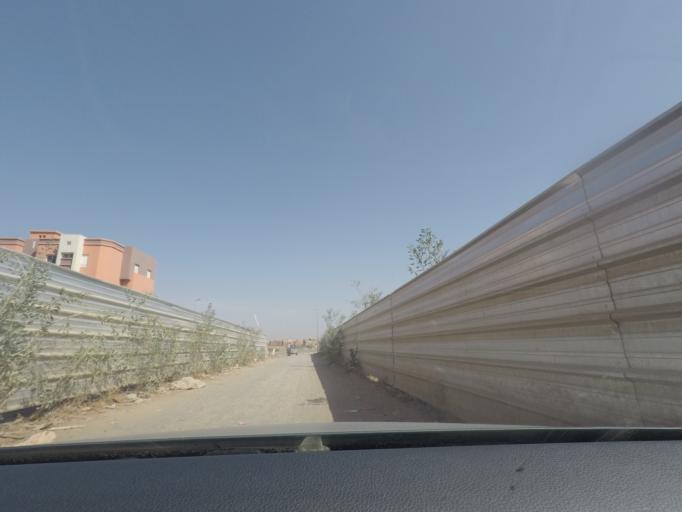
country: MA
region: Marrakech-Tensift-Al Haouz
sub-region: Marrakech
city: Marrakesh
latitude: 31.5863
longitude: -8.0306
